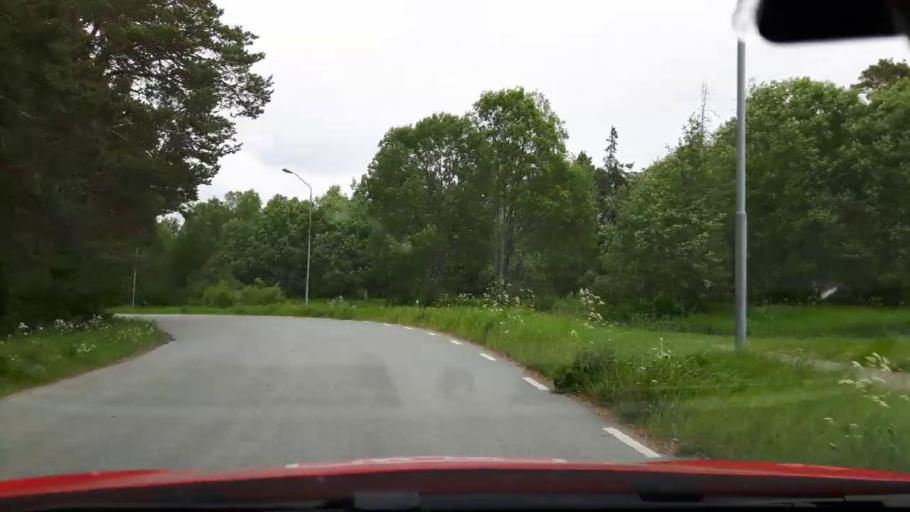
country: SE
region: Jaemtland
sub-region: OEstersunds Kommun
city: Ostersund
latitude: 63.1970
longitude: 14.6398
